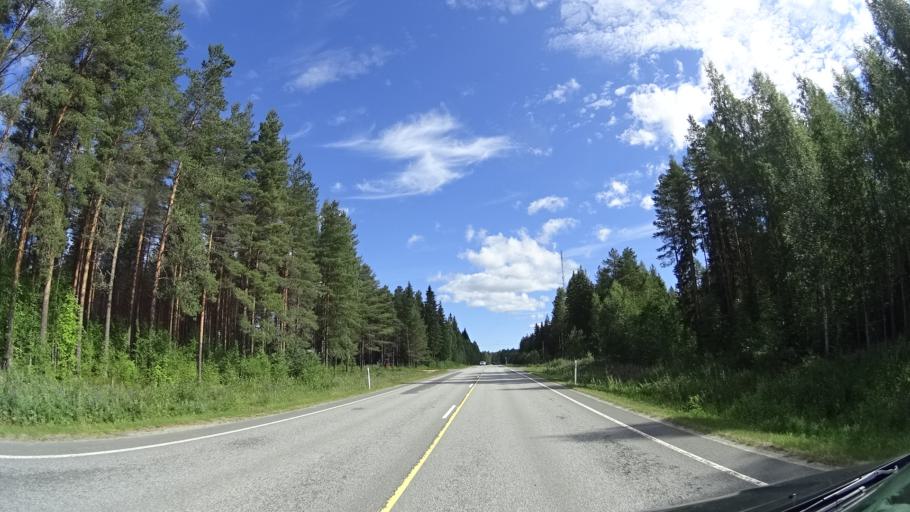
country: FI
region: Pirkanmaa
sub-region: Luoteis-Pirkanmaa
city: Kihnioe
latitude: 62.1485
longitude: 23.1552
